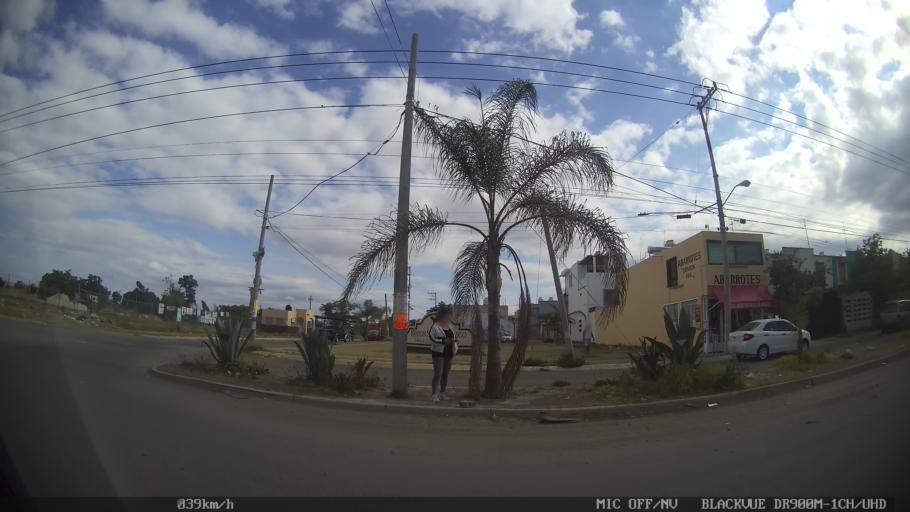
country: MX
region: Jalisco
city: Tonala
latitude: 20.6592
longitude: -103.2477
